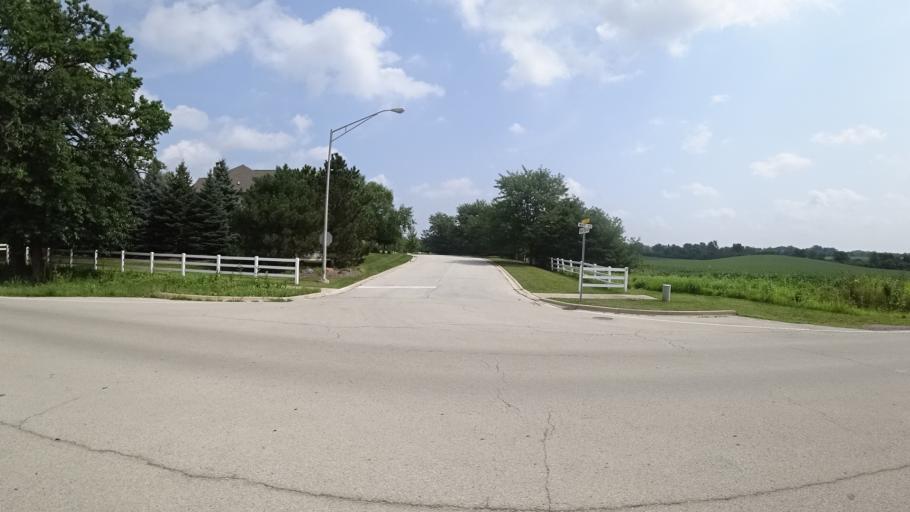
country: US
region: Illinois
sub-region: Cook County
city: Orland Park
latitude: 41.6250
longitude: -87.8922
